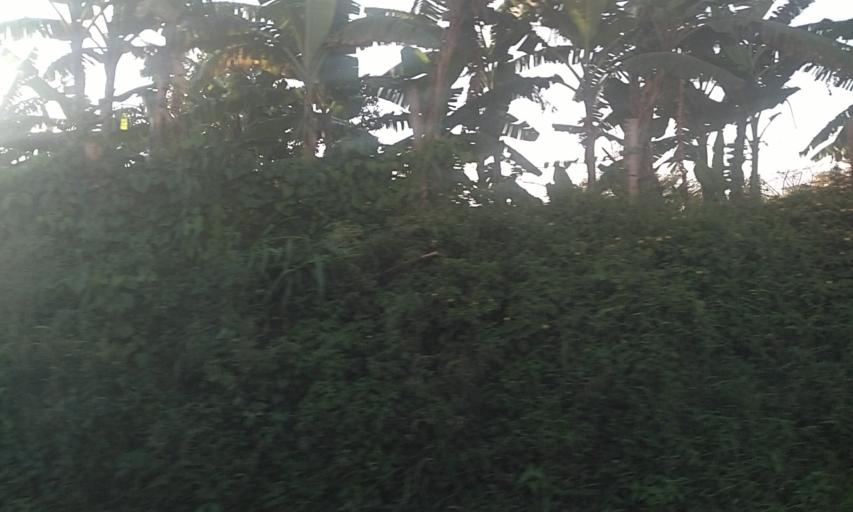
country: UG
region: Central Region
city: Kampala Central Division
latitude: 0.3162
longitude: 32.5615
